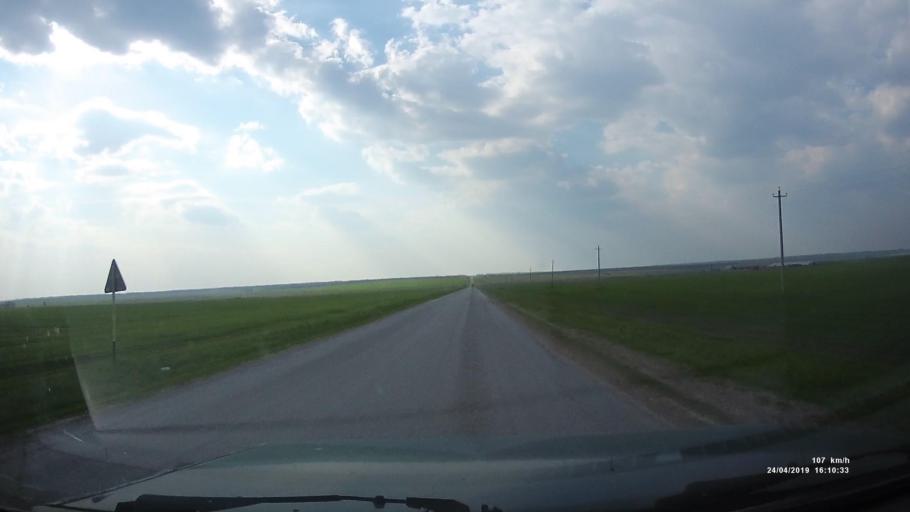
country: RU
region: Rostov
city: Sovetskoye
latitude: 46.7181
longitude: 42.2684
